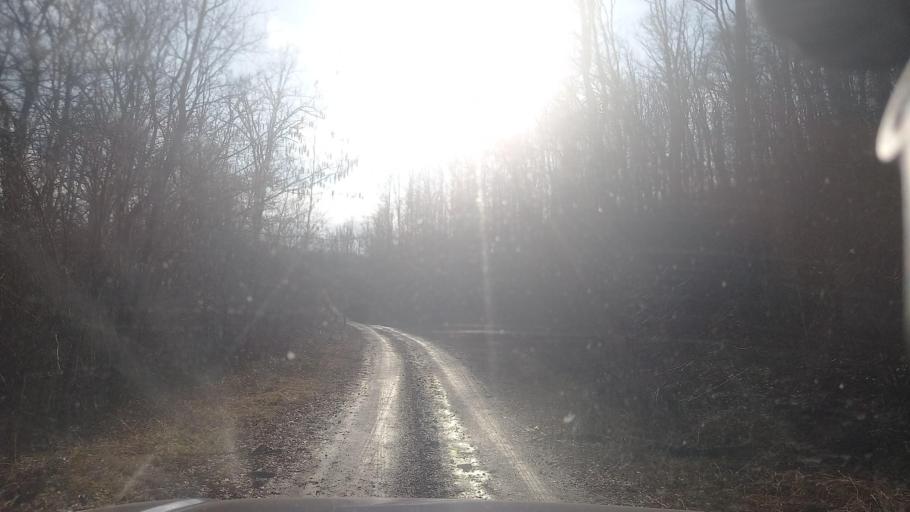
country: RU
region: Krasnodarskiy
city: Smolenskaya
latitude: 44.6837
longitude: 38.7809
